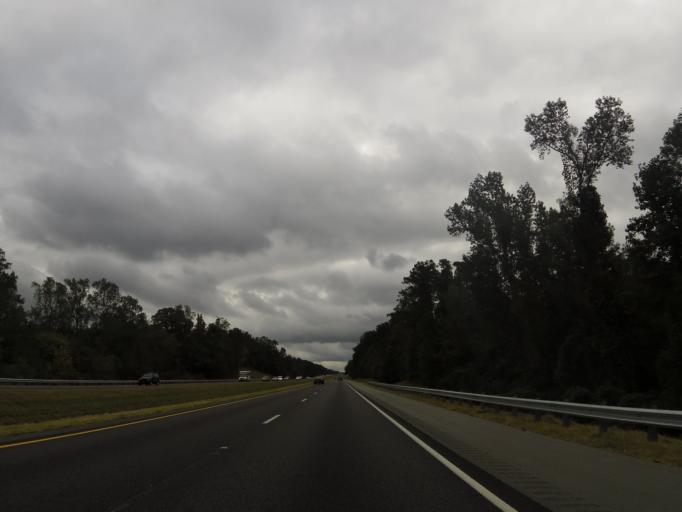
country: US
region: Alabama
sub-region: Conecuh County
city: Evergreen
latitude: 31.4814
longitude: -86.9454
